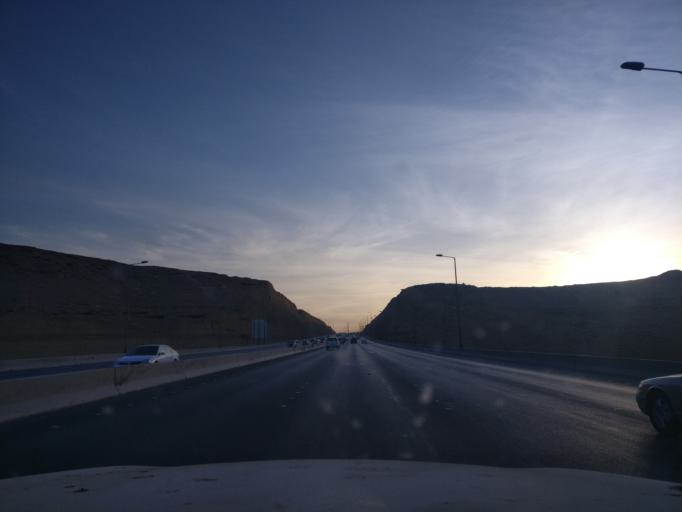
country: SA
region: Ar Riyad
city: Riyadh
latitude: 24.6122
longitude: 46.5652
